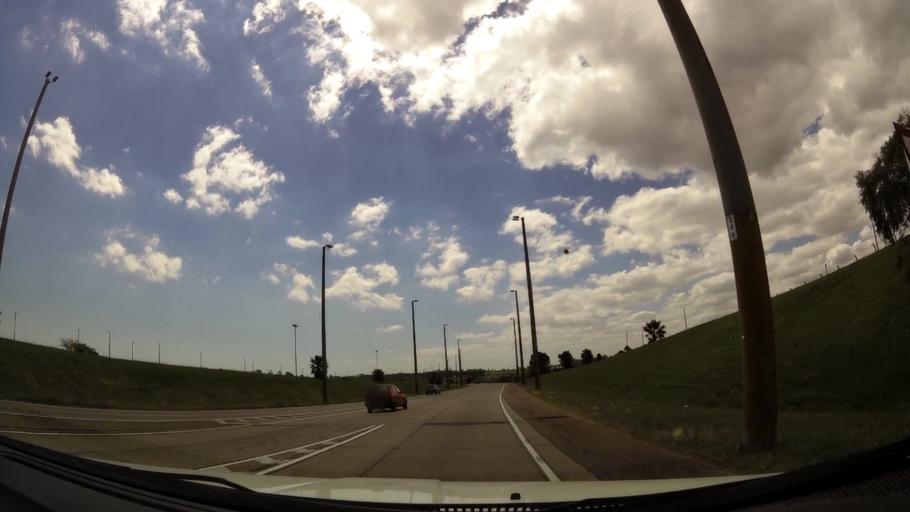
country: UY
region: Canelones
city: La Paz
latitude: -34.8225
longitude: -56.2517
